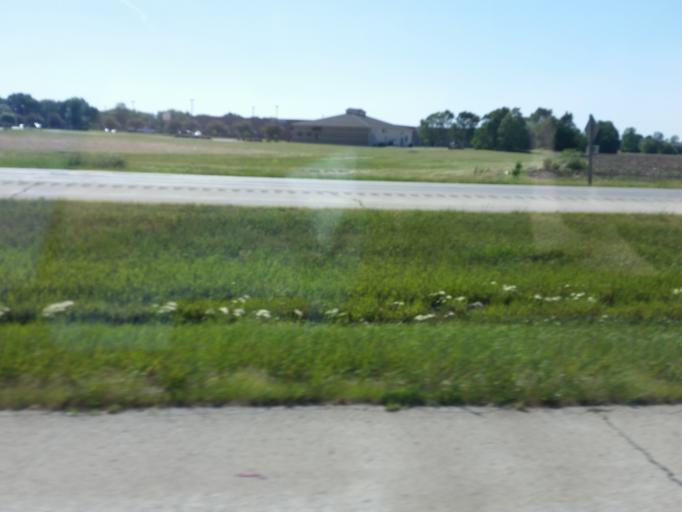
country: US
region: Illinois
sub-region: Winnebago County
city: Roscoe
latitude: 42.4315
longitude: -89.0161
